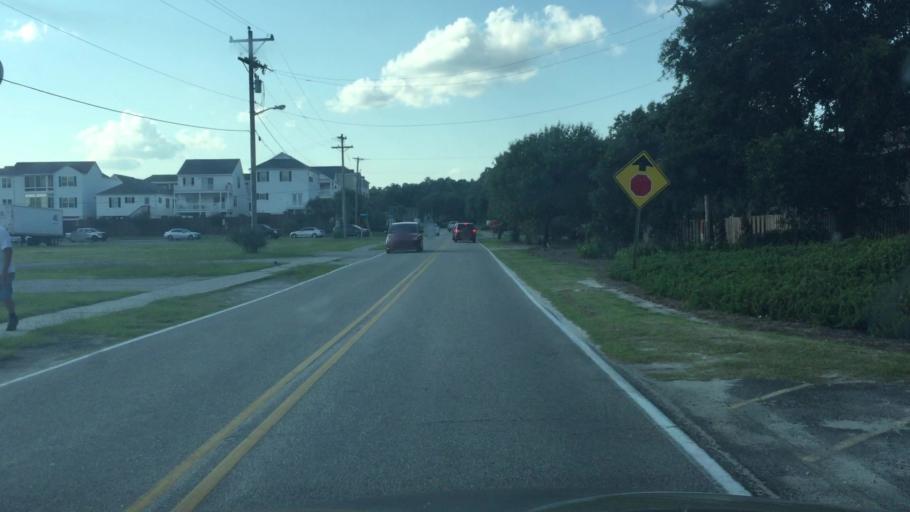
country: US
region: South Carolina
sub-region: Horry County
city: North Myrtle Beach
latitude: 33.8203
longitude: -78.6705
